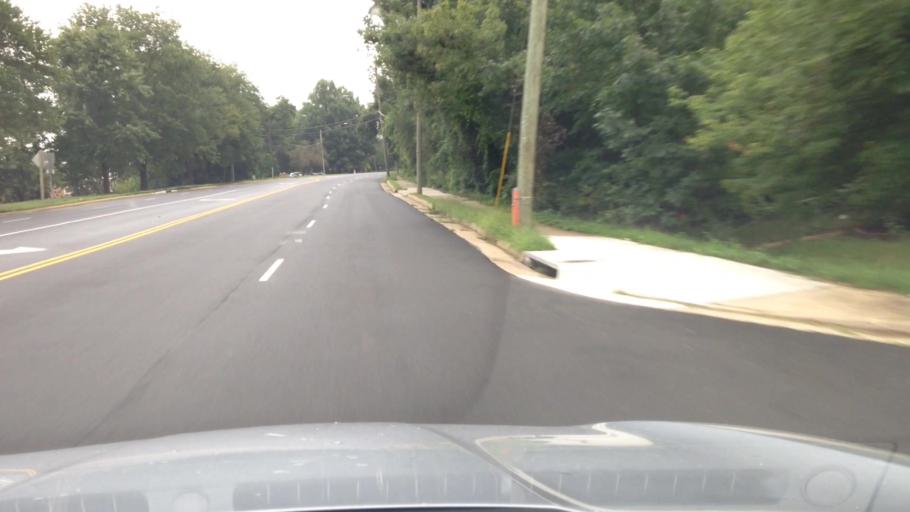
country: US
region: Virginia
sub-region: Fairfax County
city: Huntington
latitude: 38.7957
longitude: -77.0791
